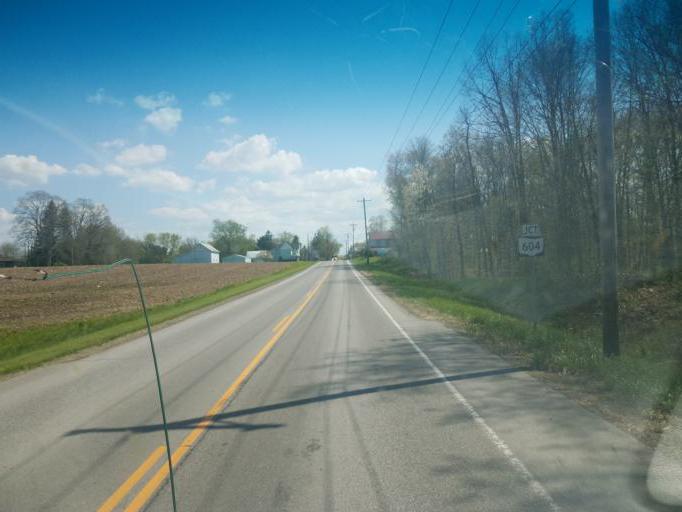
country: US
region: Ohio
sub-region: Wayne County
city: West Salem
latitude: 40.9193
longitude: -82.1090
